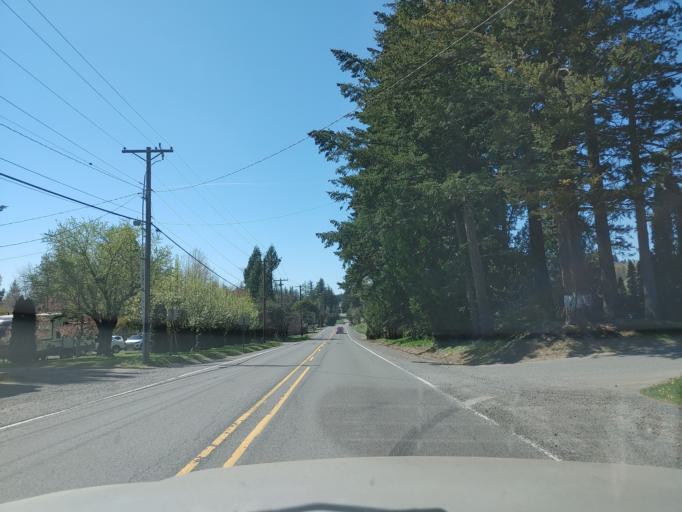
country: US
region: Oregon
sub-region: Multnomah County
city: Troutdale
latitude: 45.5190
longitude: -122.3307
